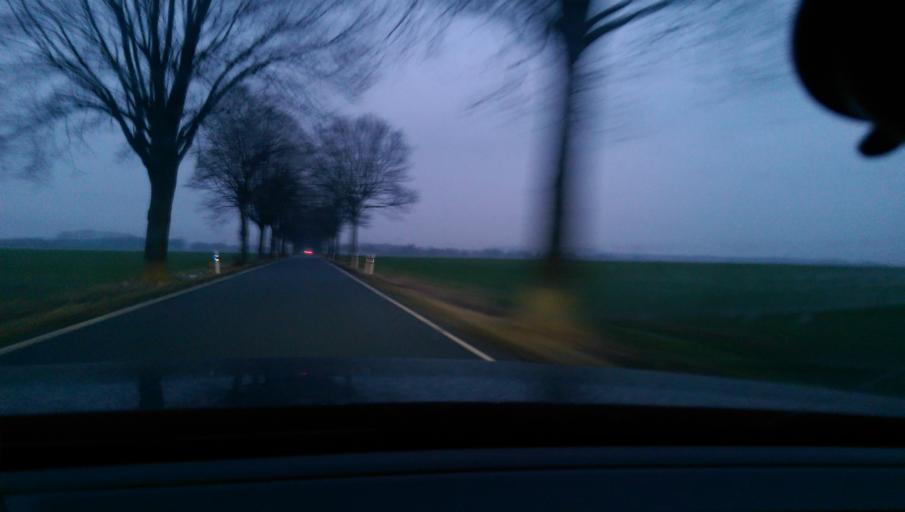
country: DE
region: Lower Saxony
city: Wennigsen
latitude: 52.3096
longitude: 9.5632
